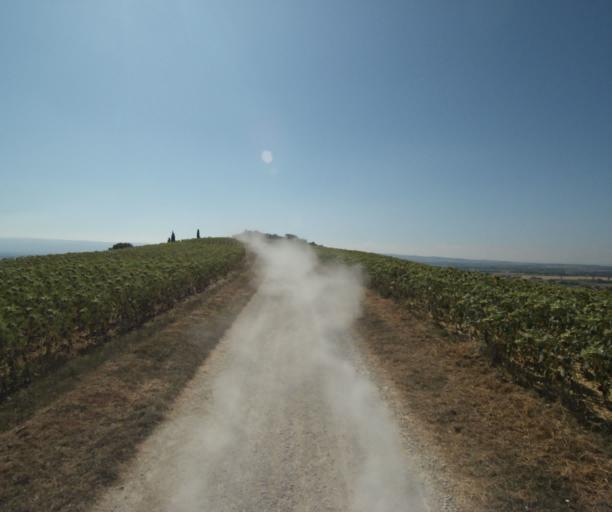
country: FR
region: Midi-Pyrenees
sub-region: Departement de la Haute-Garonne
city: Saint-Felix-Lauragais
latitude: 43.5030
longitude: 1.9347
